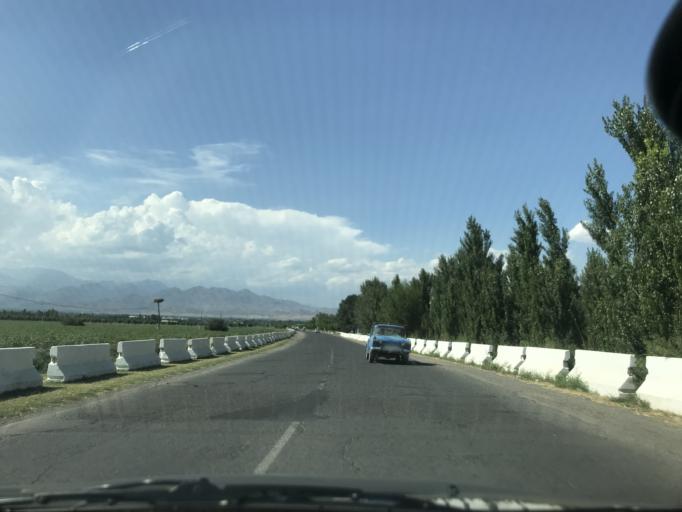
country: UZ
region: Namangan
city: Chust Shahri
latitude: 41.0362
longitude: 71.2128
